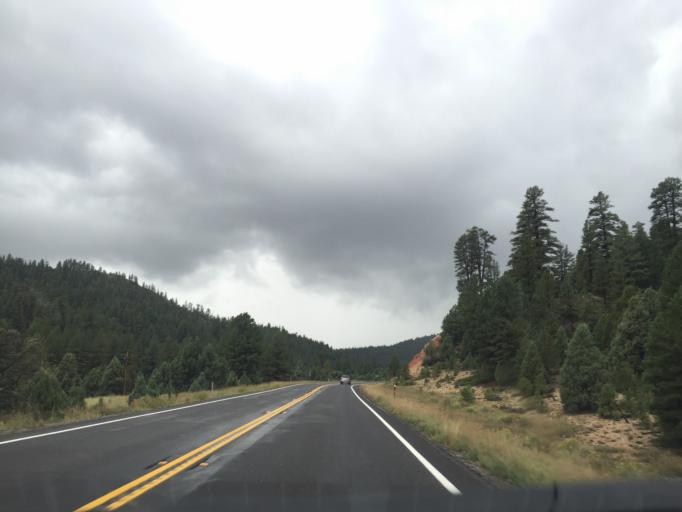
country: US
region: Utah
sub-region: Garfield County
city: Panguitch
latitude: 37.4547
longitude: -112.5270
